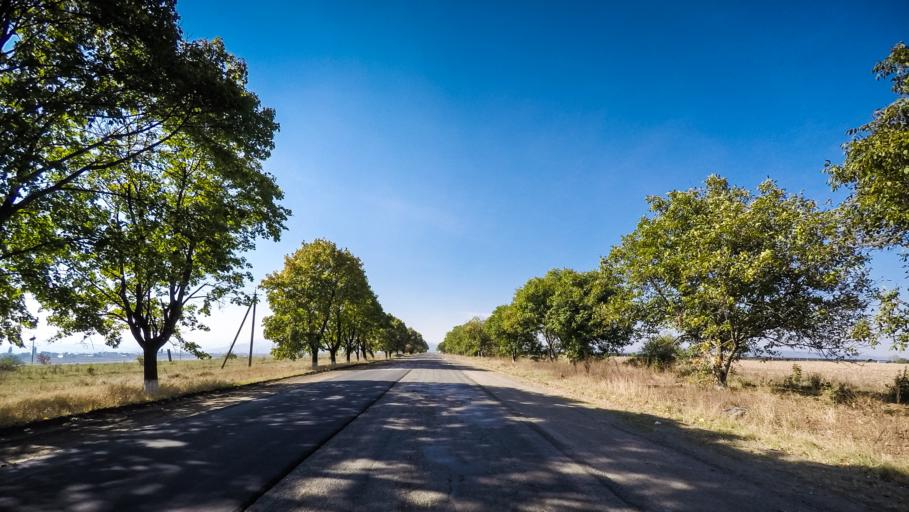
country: RU
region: Kabardino-Balkariya
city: Shalushka
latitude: 43.5750
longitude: 43.5609
